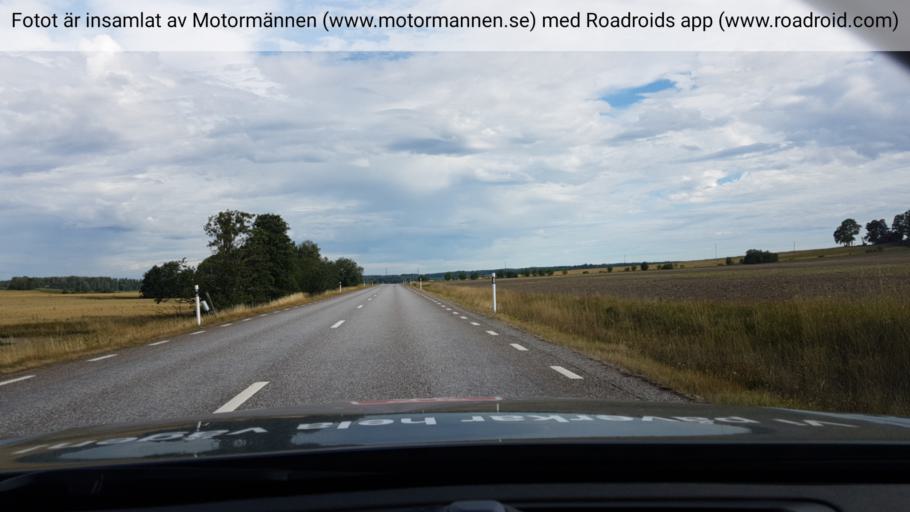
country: SE
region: Uppsala
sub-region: Enkopings Kommun
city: Irsta
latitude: 59.8150
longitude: 16.9218
